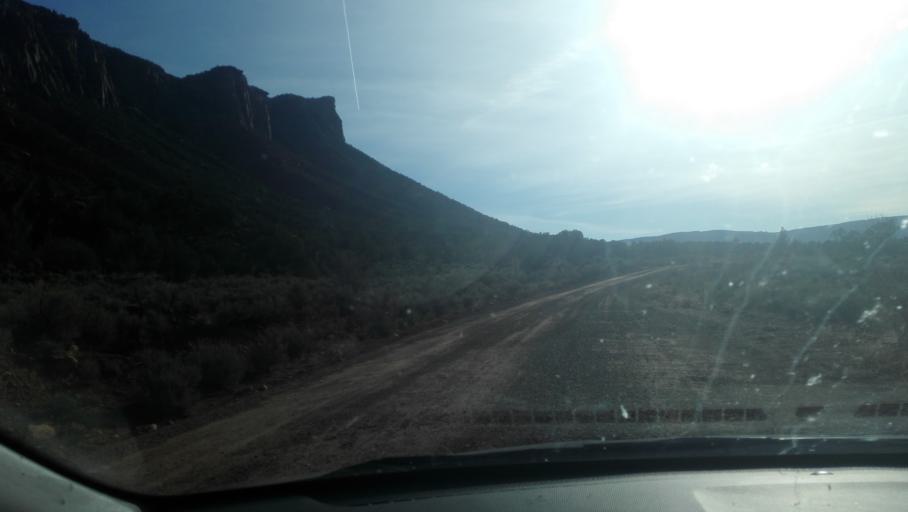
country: US
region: Colorado
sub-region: Dolores County
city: Dove Creek
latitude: 38.3580
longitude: -108.8296
